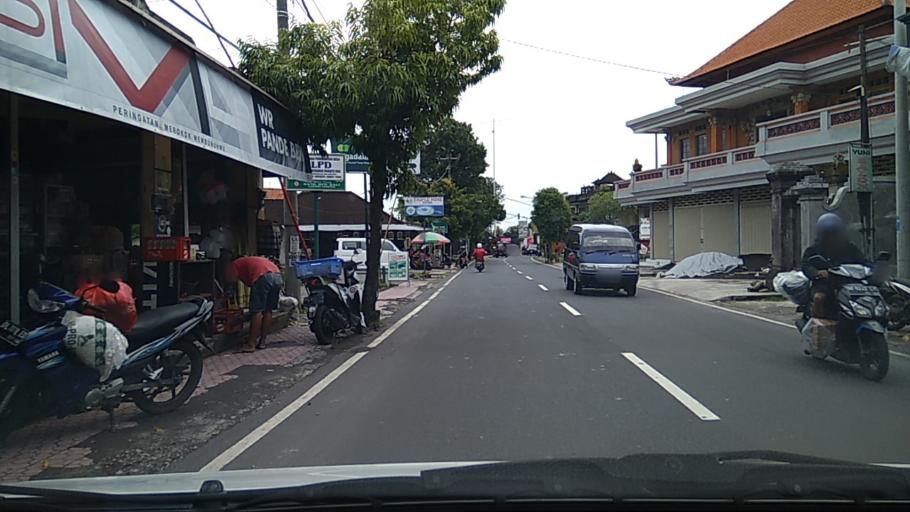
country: ID
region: Bali
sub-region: Kabupaten Gianyar
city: Ubud
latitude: -8.5323
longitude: 115.3017
